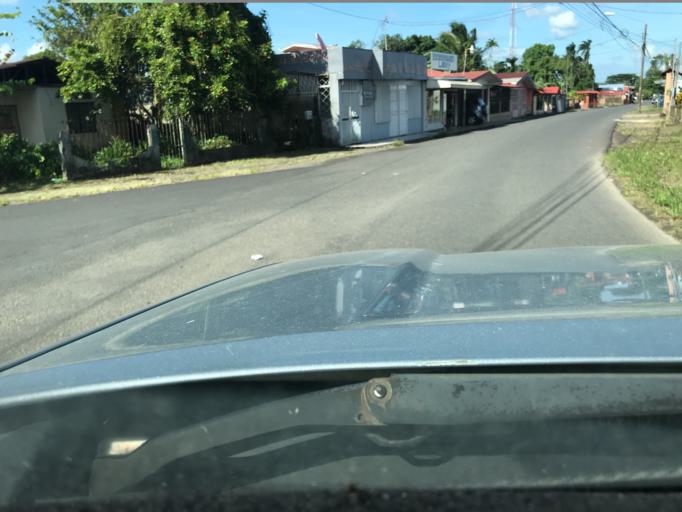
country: CR
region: Limon
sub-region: Canton de Guacimo
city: Guacimo
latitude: 10.2097
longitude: -83.6799
